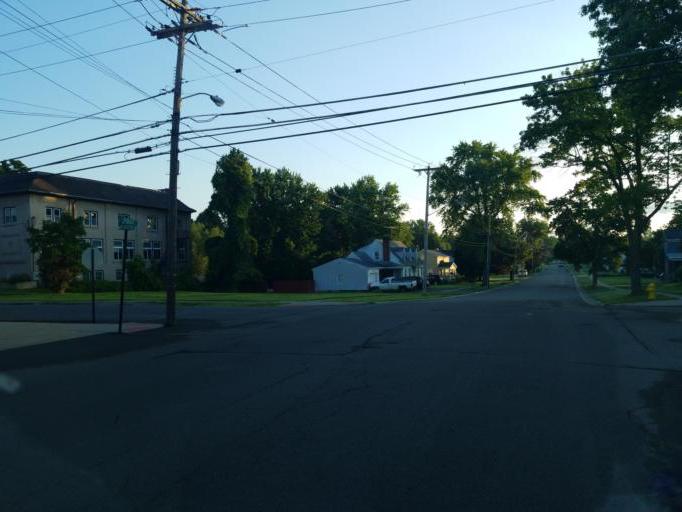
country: US
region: New York
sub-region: Wayne County
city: Clyde
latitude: 43.0865
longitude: -76.8699
